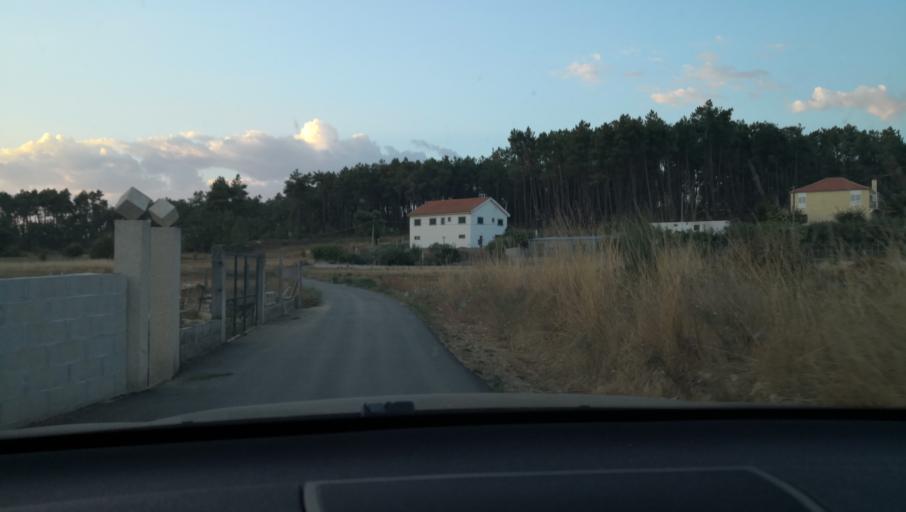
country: PT
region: Vila Real
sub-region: Sabrosa
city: Vilela
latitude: 41.2254
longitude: -7.6061
